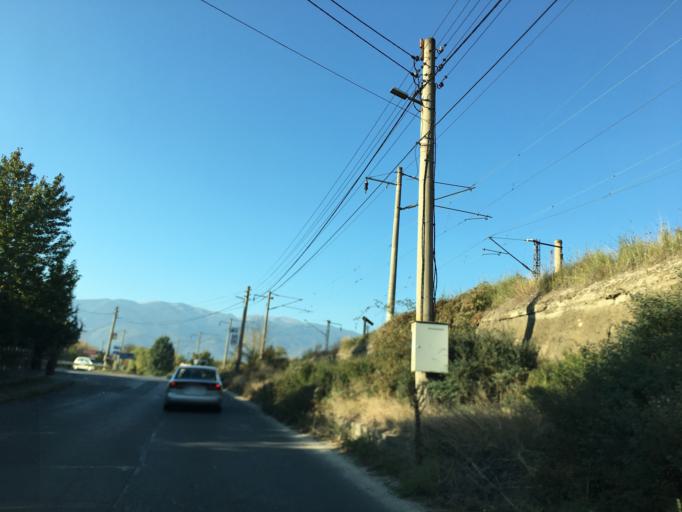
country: BG
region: Sofiya
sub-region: Obshtina Dolna Banya
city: Dolna Banya
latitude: 42.3166
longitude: 23.8576
